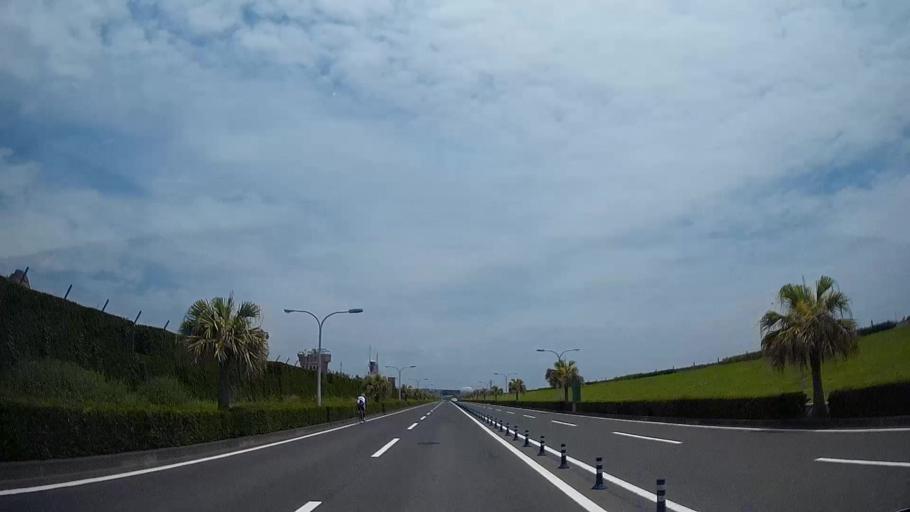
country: JP
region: Tokyo
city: Urayasu
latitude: 35.6240
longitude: 139.8814
